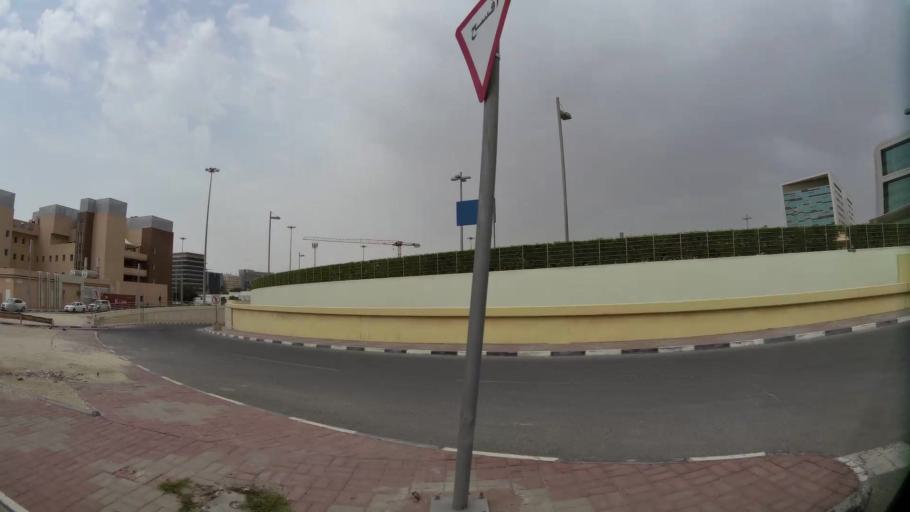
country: QA
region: Baladiyat ad Dawhah
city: Doha
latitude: 25.2934
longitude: 51.5089
